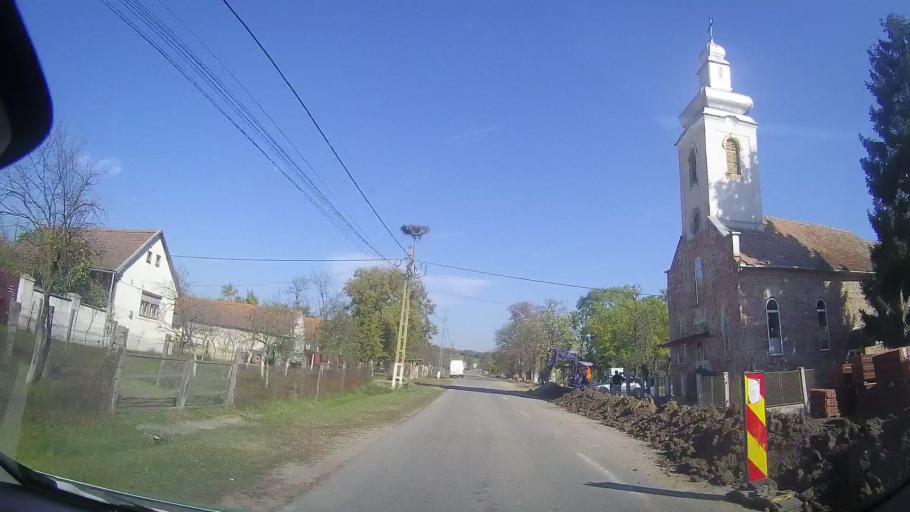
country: RO
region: Timis
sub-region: Comuna Secas
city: Secas
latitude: 45.8477
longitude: 21.7932
